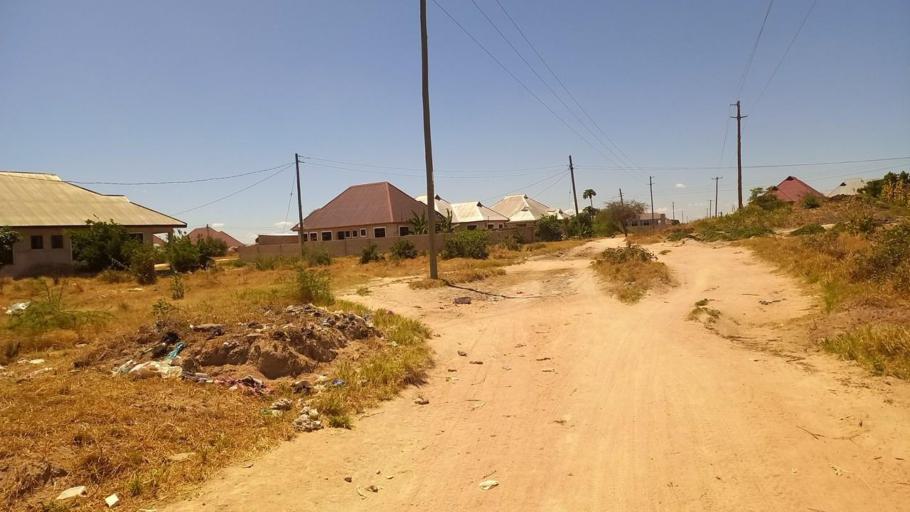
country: TZ
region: Dodoma
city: Dodoma
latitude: -6.1344
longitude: 35.7138
